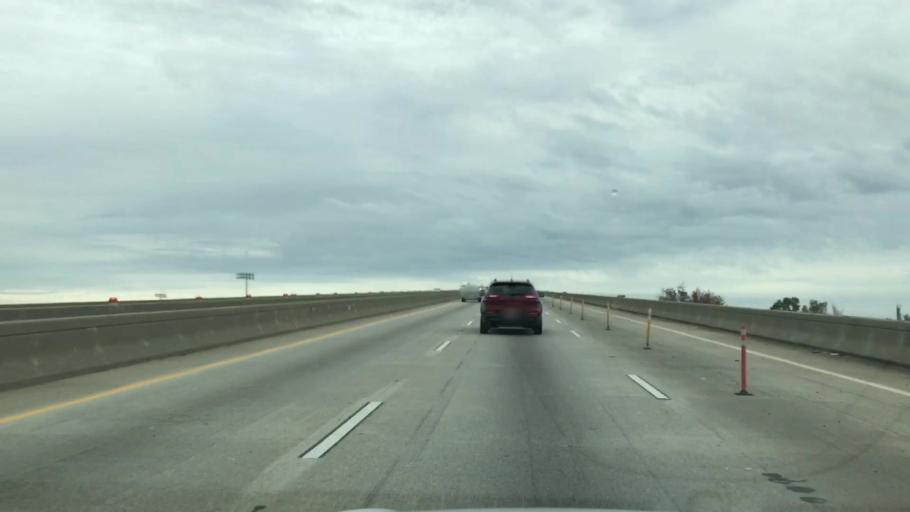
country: US
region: South Carolina
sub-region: Charleston County
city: North Charleston
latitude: 32.8644
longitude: -79.9034
